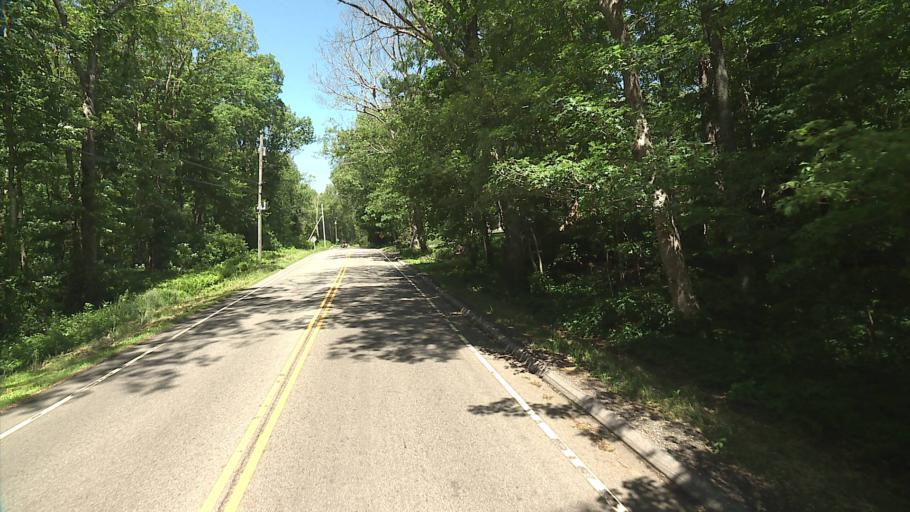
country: US
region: Rhode Island
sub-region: Washington County
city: Hopkinton
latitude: 41.5006
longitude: -71.8343
